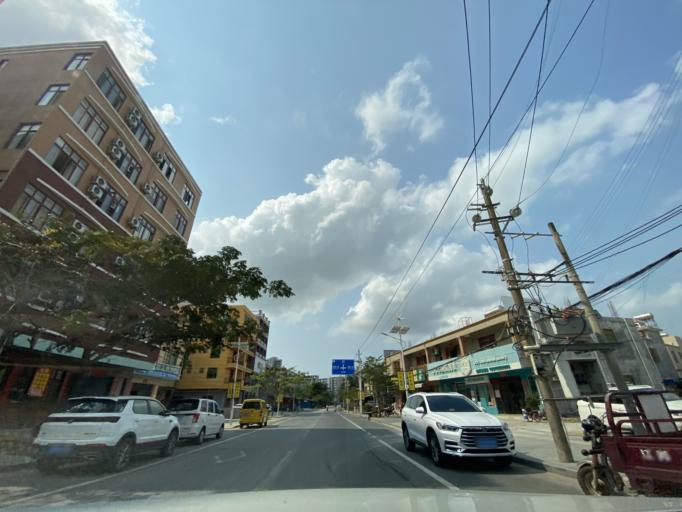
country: CN
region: Hainan
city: Yingzhou
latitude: 18.4201
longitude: 109.8498
